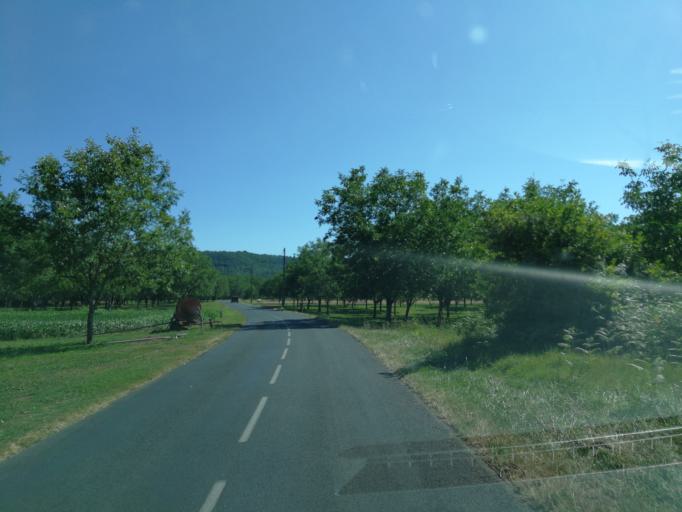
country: FR
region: Midi-Pyrenees
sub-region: Departement du Lot
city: Souillac
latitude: 44.8783
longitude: 1.4461
